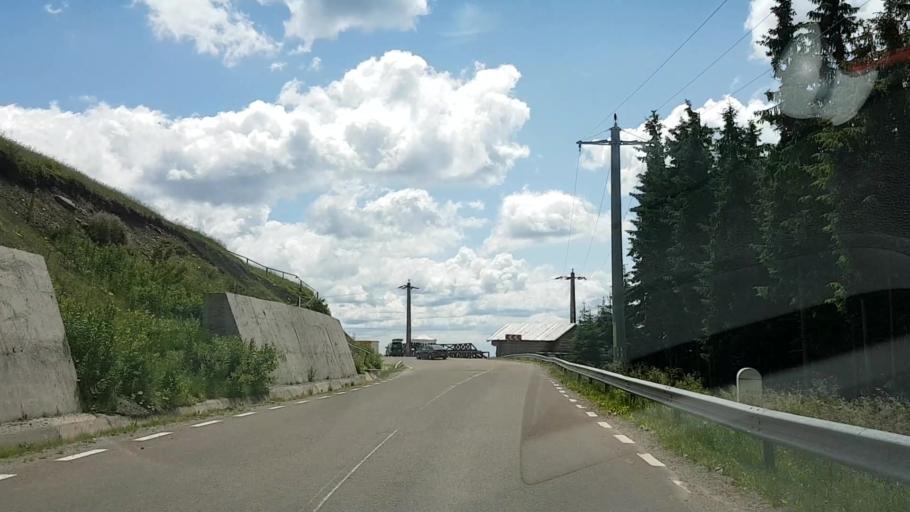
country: RO
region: Suceava
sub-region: Municipiul Campulung Moldovenesc
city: Campulung Moldovenesc
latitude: 47.4541
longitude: 25.5423
